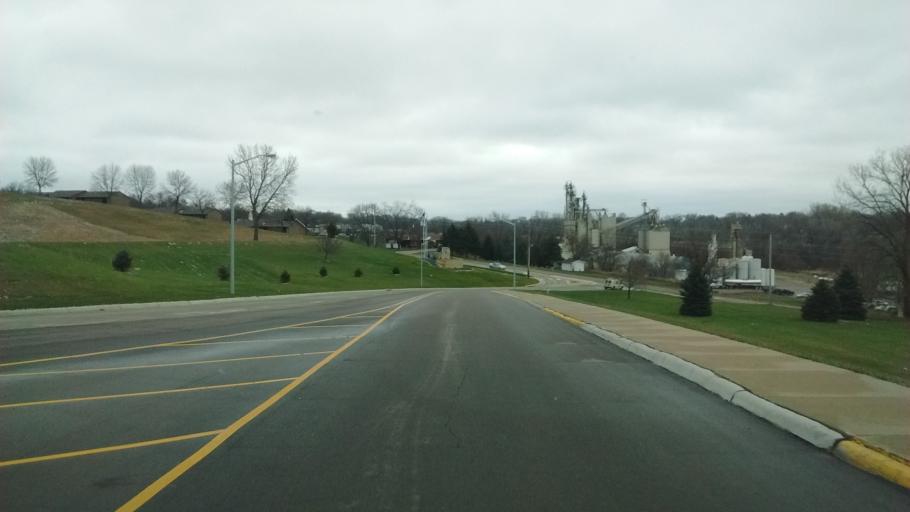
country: US
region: Iowa
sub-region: Woodbury County
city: Sioux City
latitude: 42.4806
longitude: -96.3481
